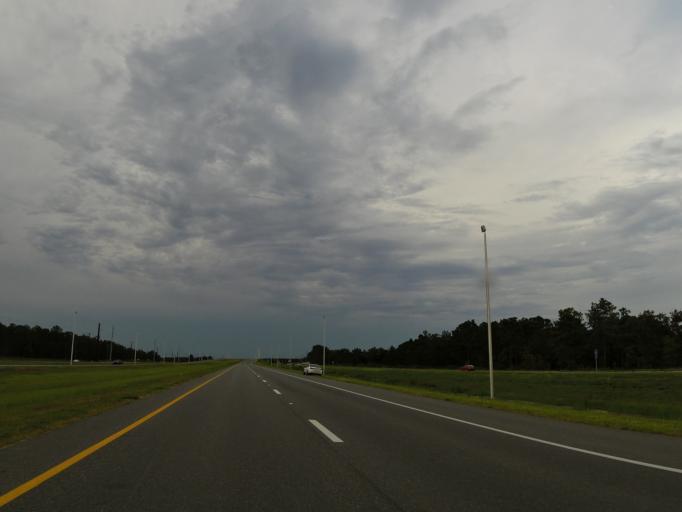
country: US
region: Florida
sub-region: Clay County
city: Lakeside
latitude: 30.1514
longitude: -81.8308
